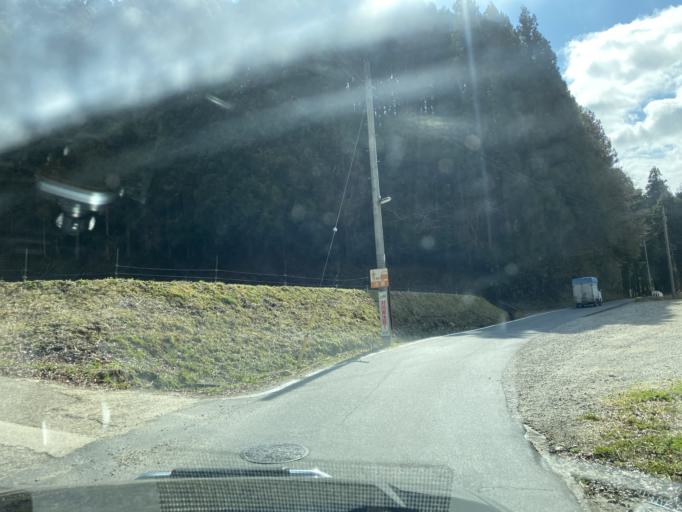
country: JP
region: Nara
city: Nara-shi
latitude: 34.7041
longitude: 135.9528
